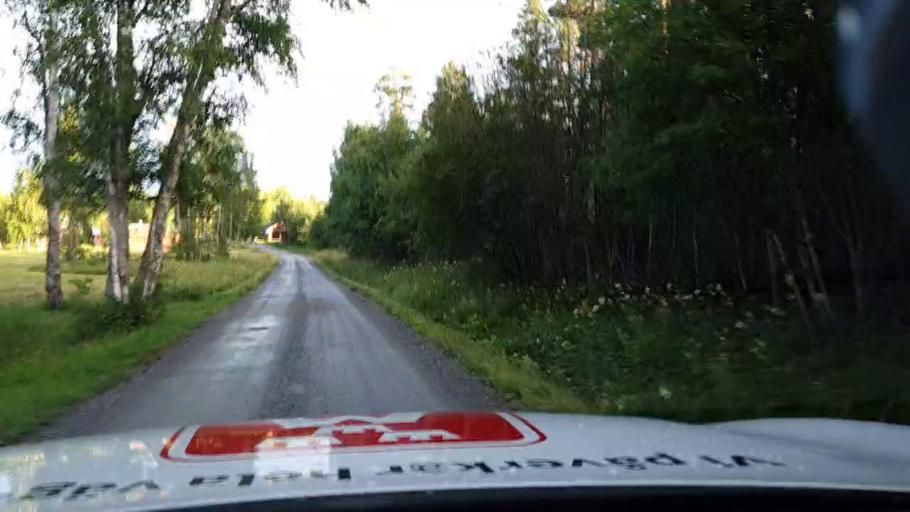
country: SE
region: Jaemtland
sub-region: Bergs Kommun
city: Hoverberg
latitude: 62.8542
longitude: 14.5367
